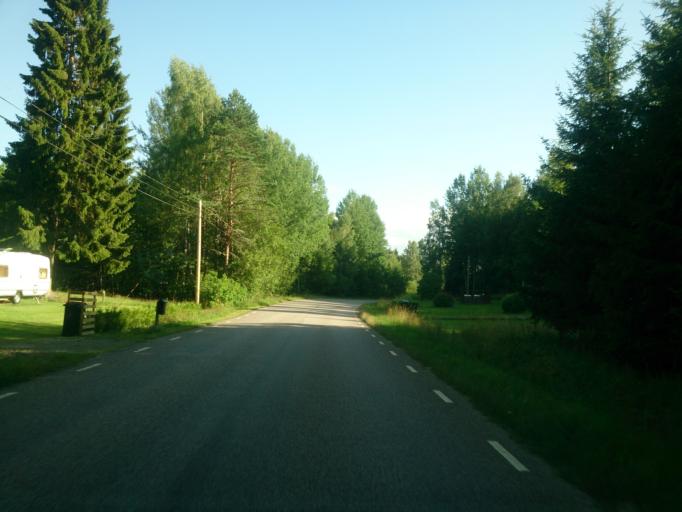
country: SE
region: OEstergoetland
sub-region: Atvidabergs Kommun
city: Atvidaberg
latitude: 58.3102
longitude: 16.0243
